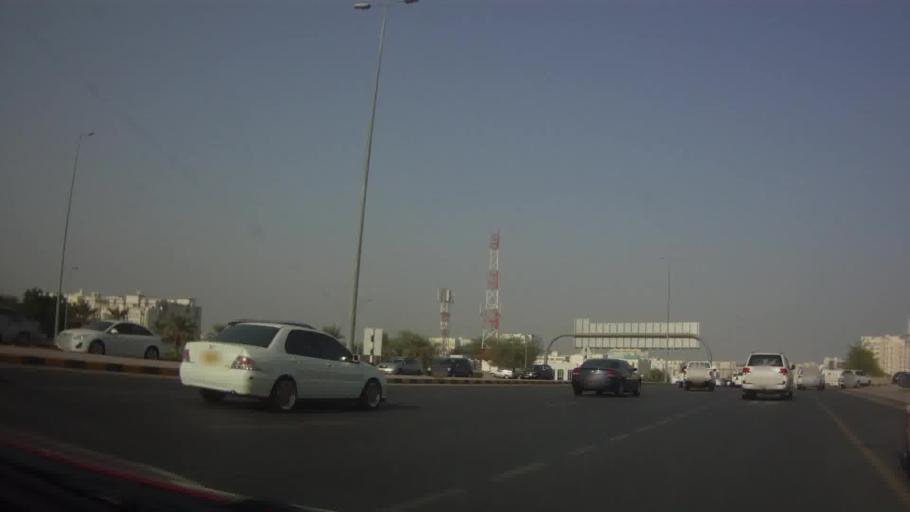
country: OM
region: Muhafazat Masqat
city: Bawshar
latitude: 23.5880
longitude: 58.4123
